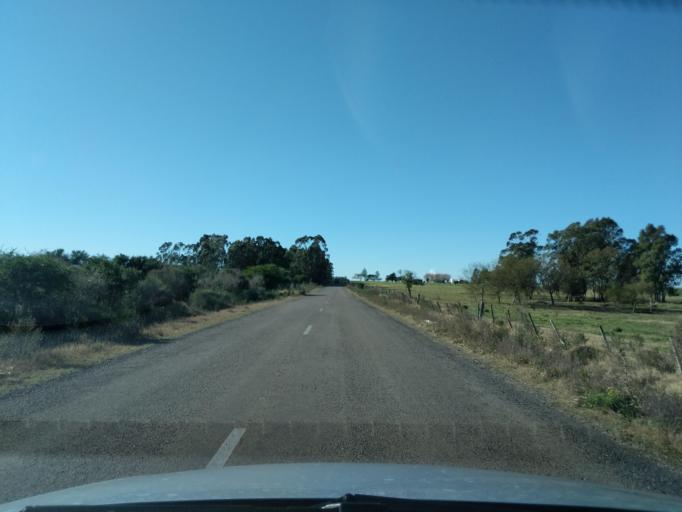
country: UY
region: Florida
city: Florida
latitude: -34.0507
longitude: -56.2512
